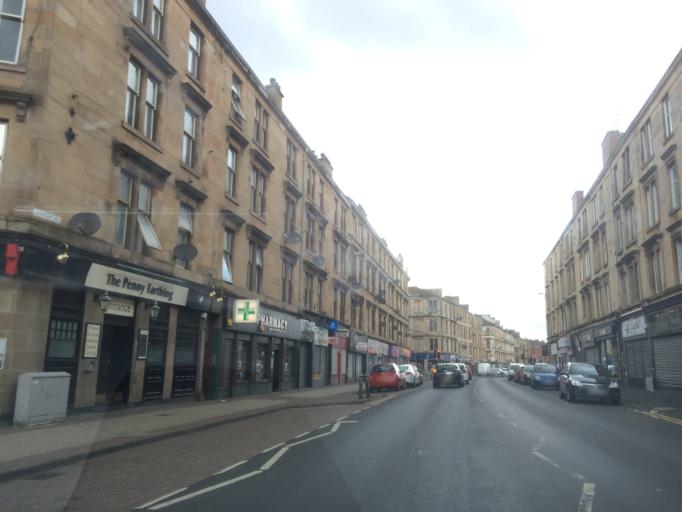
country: GB
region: Scotland
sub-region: Glasgow City
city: Glasgow
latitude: 55.8359
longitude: -4.2568
